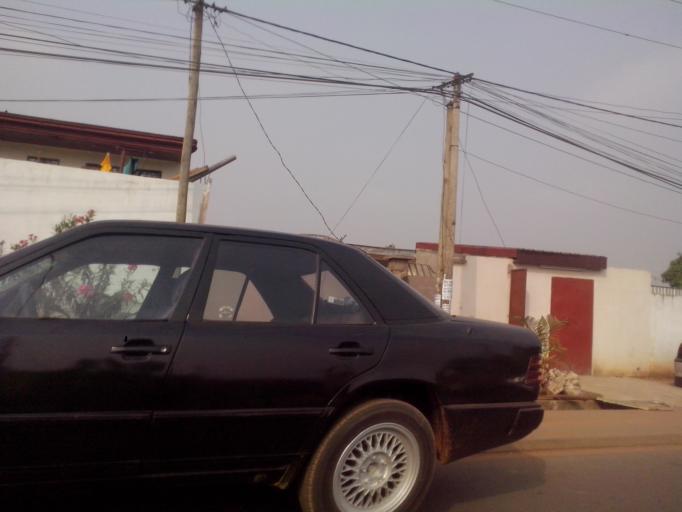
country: CM
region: Centre
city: Yaounde
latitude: 3.8479
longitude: 11.4962
